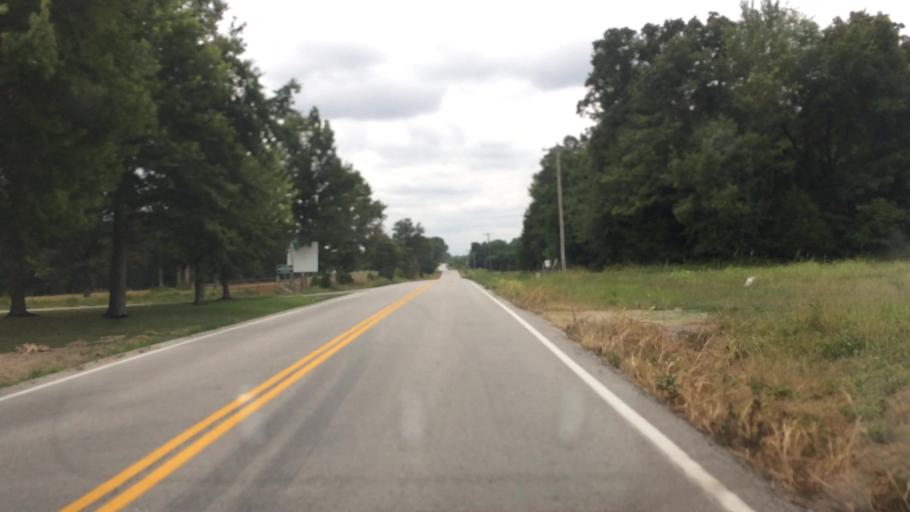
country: US
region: Missouri
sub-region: Greene County
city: Strafford
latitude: 37.2929
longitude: -93.1131
